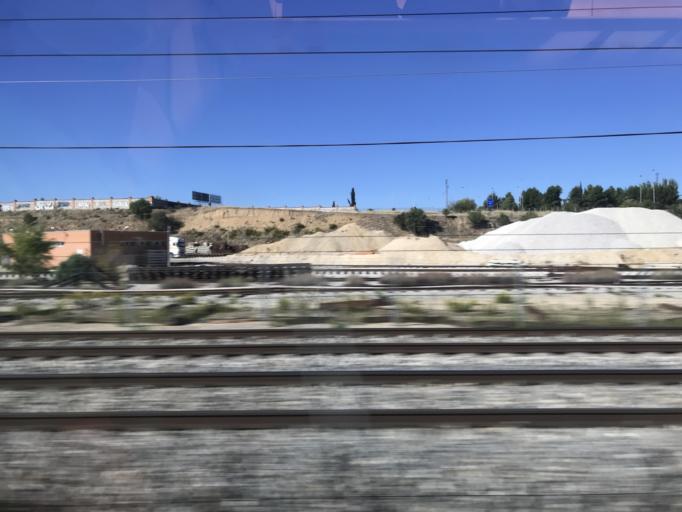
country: ES
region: Madrid
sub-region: Provincia de Madrid
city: Las Tablas
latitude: 40.5105
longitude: -3.6825
